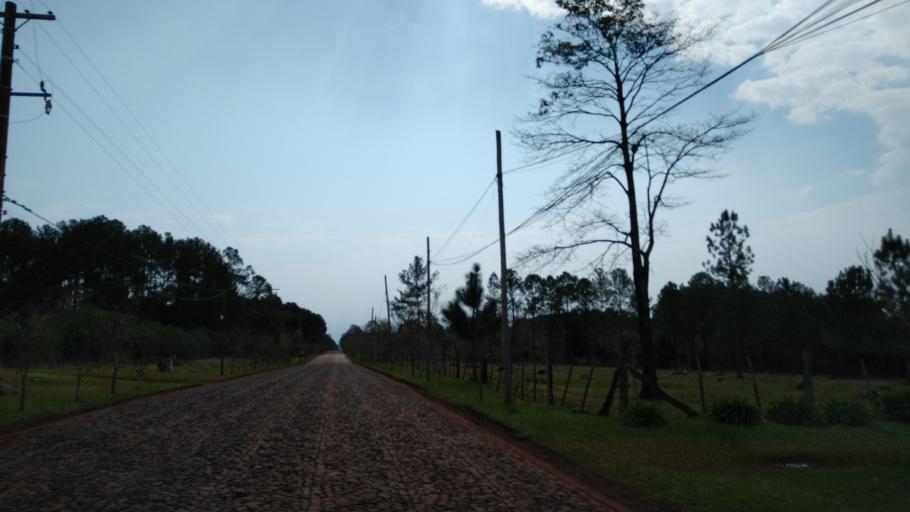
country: AR
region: Misiones
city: Ruiz de Montoya
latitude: -26.9586
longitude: -55.0561
